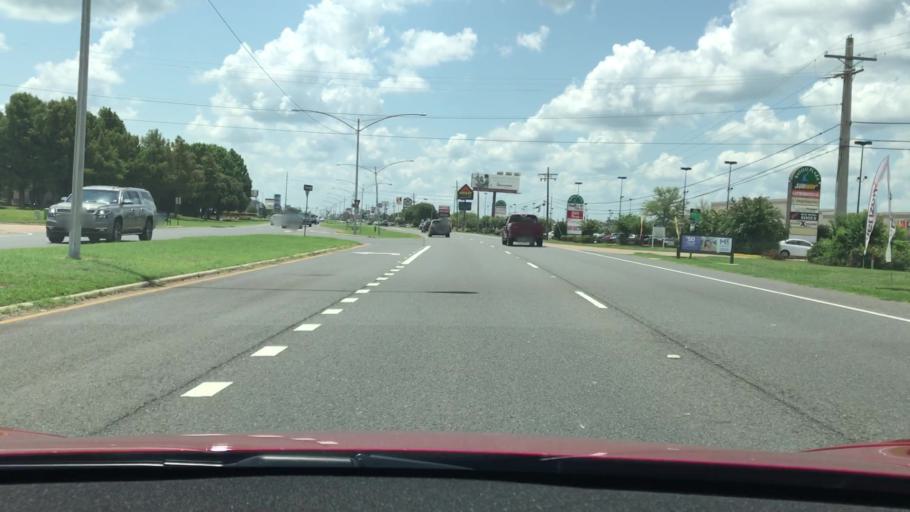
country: US
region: Louisiana
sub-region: Bossier Parish
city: Bossier City
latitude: 32.4491
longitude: -93.7218
